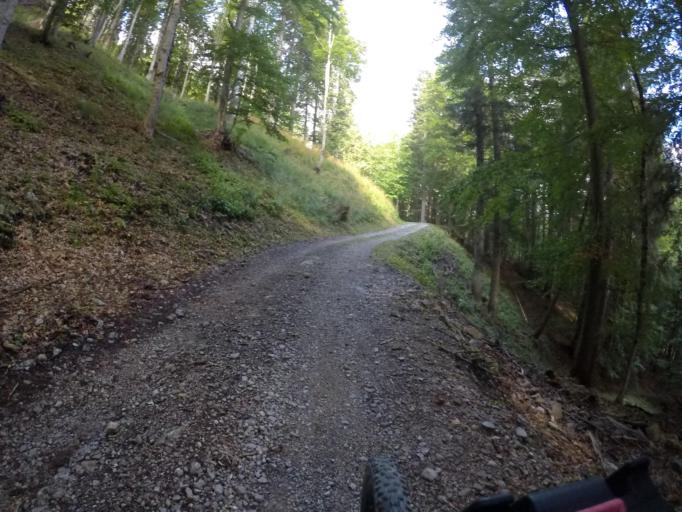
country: IT
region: Friuli Venezia Giulia
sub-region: Provincia di Udine
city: Paularo
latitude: 46.4981
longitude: 13.1746
